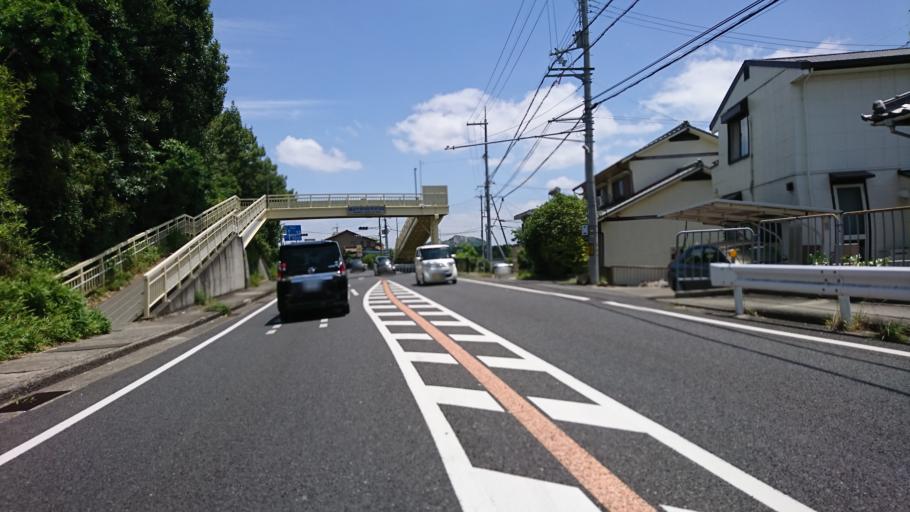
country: JP
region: Hyogo
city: Shirahamacho-usazakiminami
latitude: 34.7956
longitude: 134.7703
